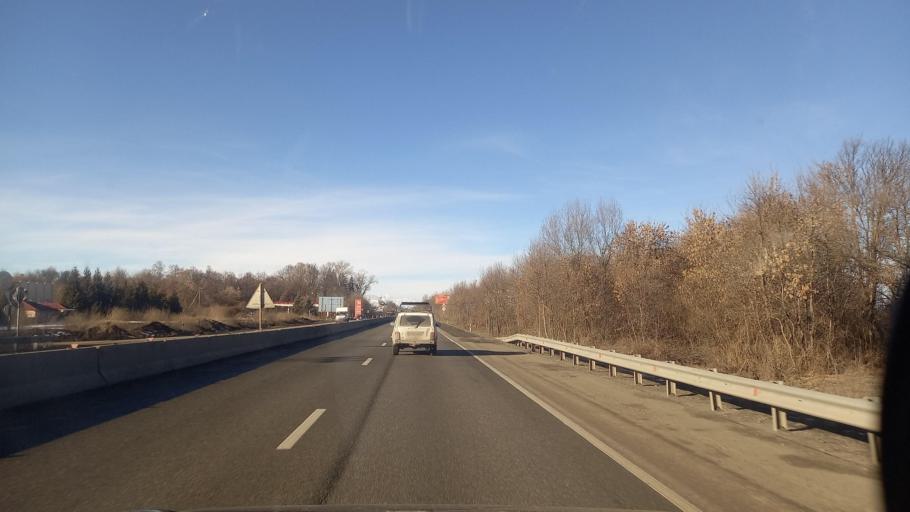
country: RU
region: North Ossetia
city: Gizel'
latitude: 43.0285
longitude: 44.5922
